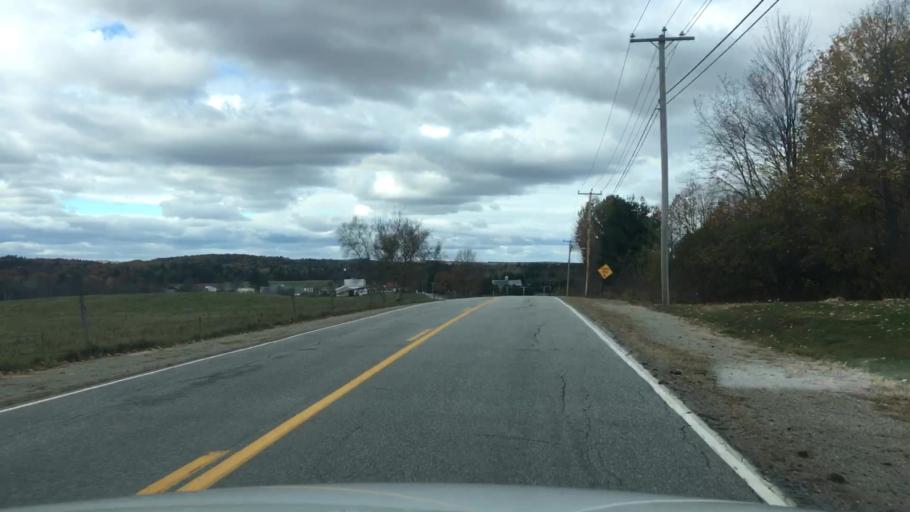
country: US
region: Maine
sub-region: Kennebec County
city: Monmouth
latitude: 44.1990
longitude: -70.0734
